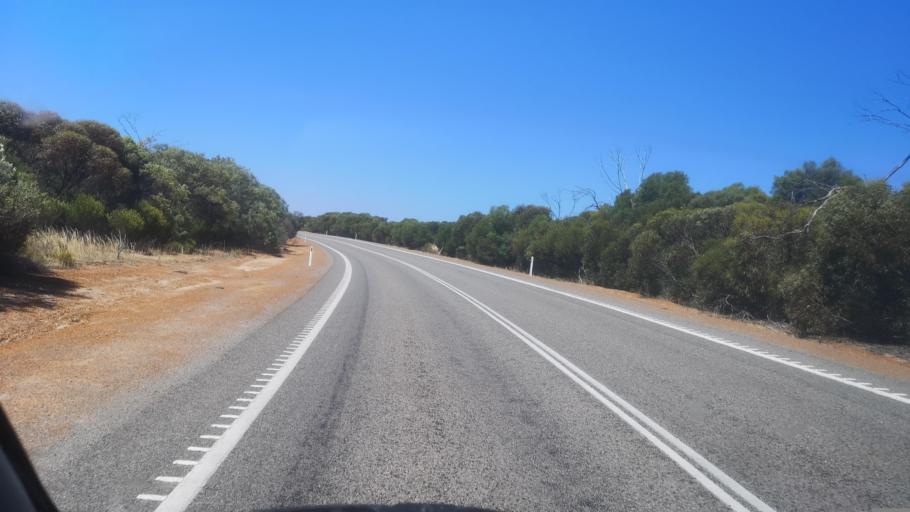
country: AU
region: Western Australia
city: Port Denison
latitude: -29.4863
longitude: 115.0107
